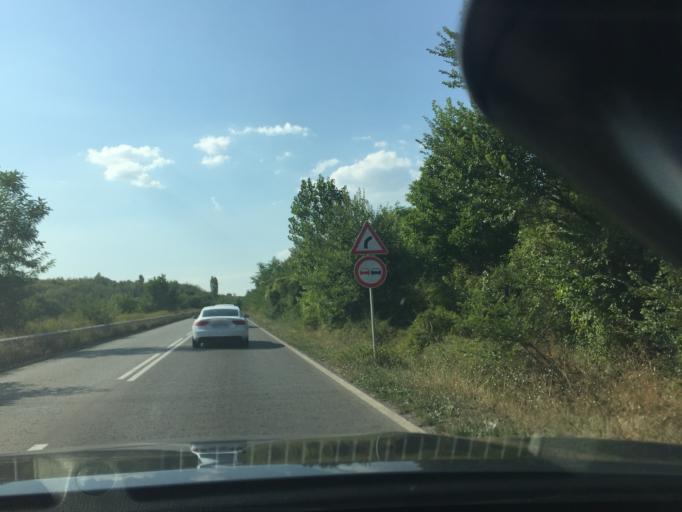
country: BG
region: Kyustendil
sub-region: Obshtina Dupnitsa
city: Dupnitsa
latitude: 42.2578
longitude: 23.0794
